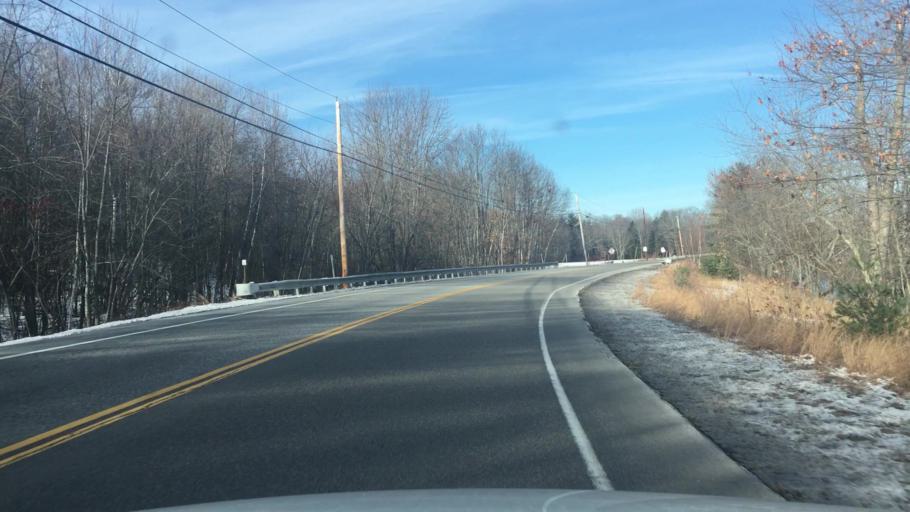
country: US
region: Maine
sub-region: Androscoggin County
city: Lisbon
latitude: 44.0092
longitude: -70.1678
